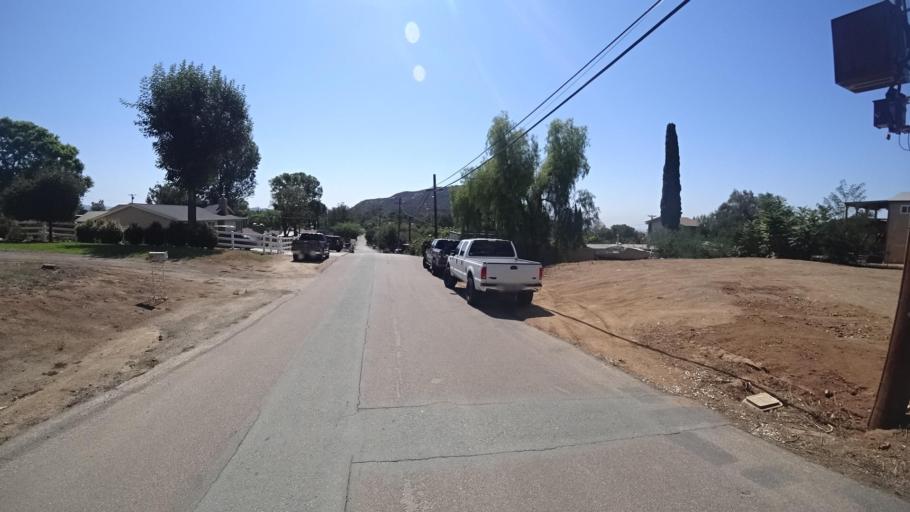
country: US
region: California
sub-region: San Diego County
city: Crest
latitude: 32.8058
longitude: -116.8693
